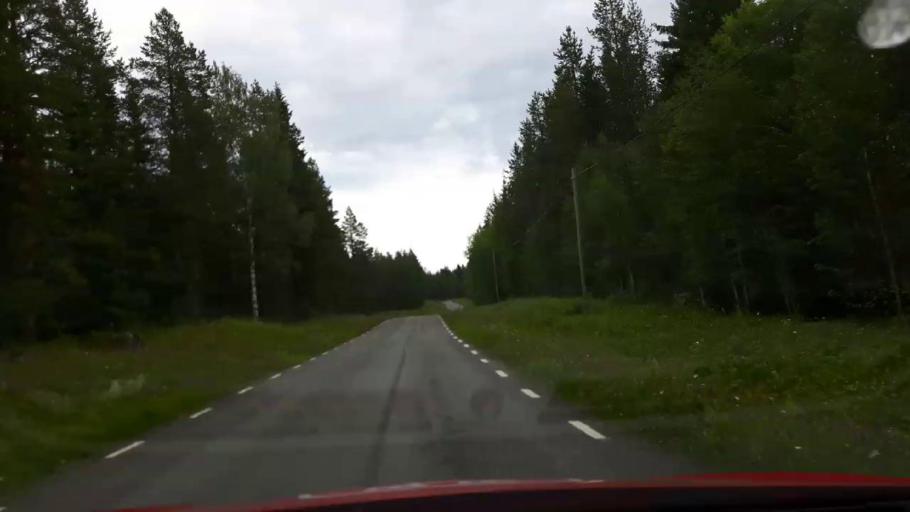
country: SE
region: Jaemtland
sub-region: OEstersunds Kommun
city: Lit
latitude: 63.3766
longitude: 15.0934
